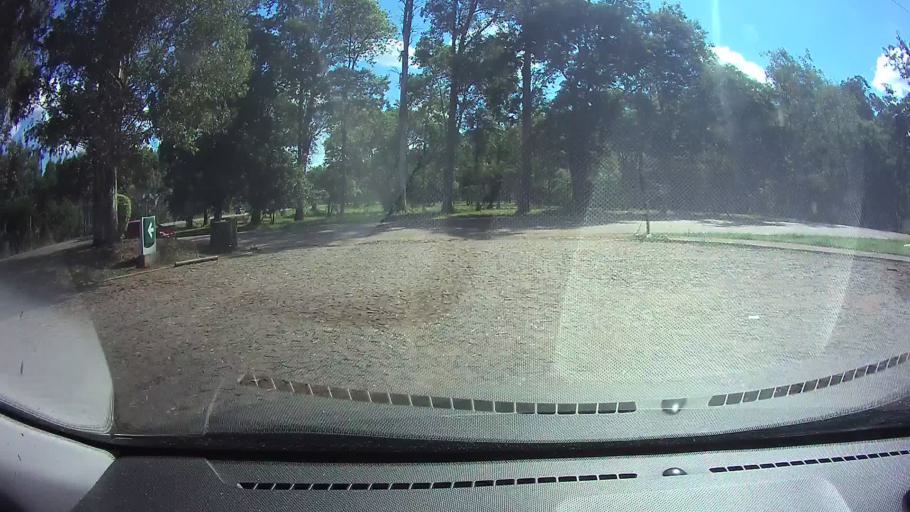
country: PY
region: Guaira
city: Coronel Martinez
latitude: -25.7660
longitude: -56.6537
